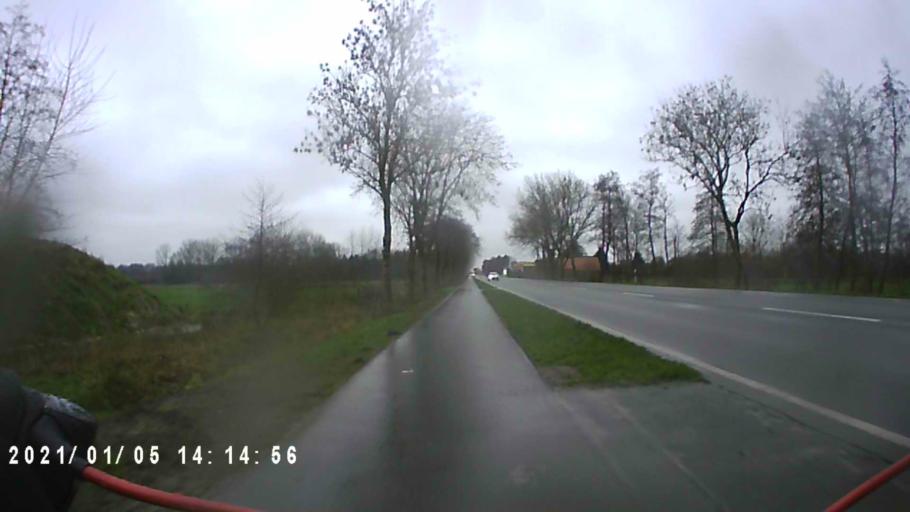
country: DE
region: Lower Saxony
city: Weener
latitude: 53.1735
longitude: 7.3154
